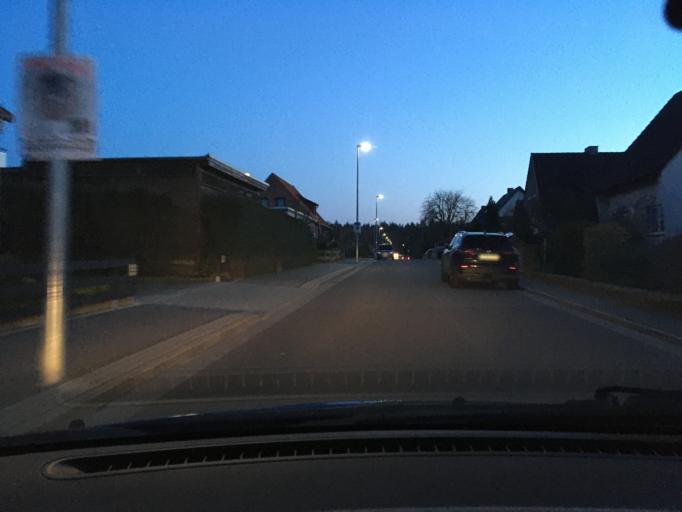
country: DE
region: Lower Saxony
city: Barum
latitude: 52.9947
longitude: 10.5084
